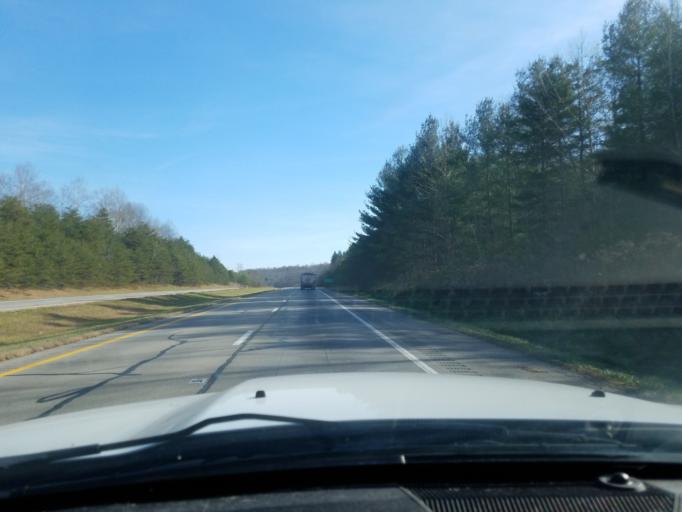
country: US
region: Ohio
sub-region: Pike County
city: Piketon
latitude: 39.0611
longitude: -83.1070
